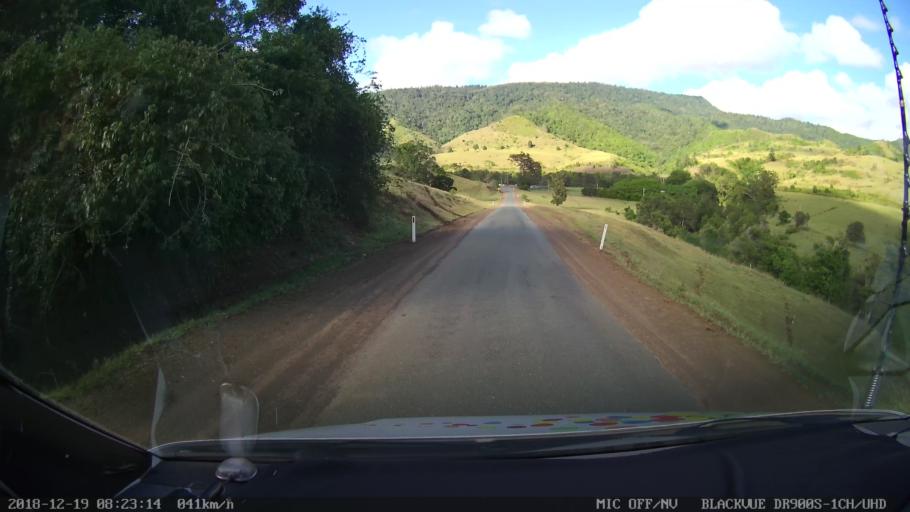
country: AU
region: New South Wales
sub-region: Kyogle
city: Kyogle
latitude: -28.3060
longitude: 152.9106
